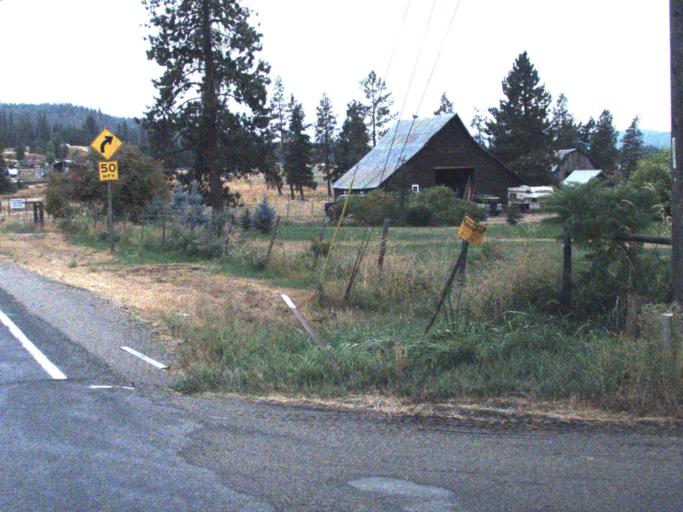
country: US
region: Washington
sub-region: Stevens County
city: Chewelah
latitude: 48.1500
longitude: -117.7261
